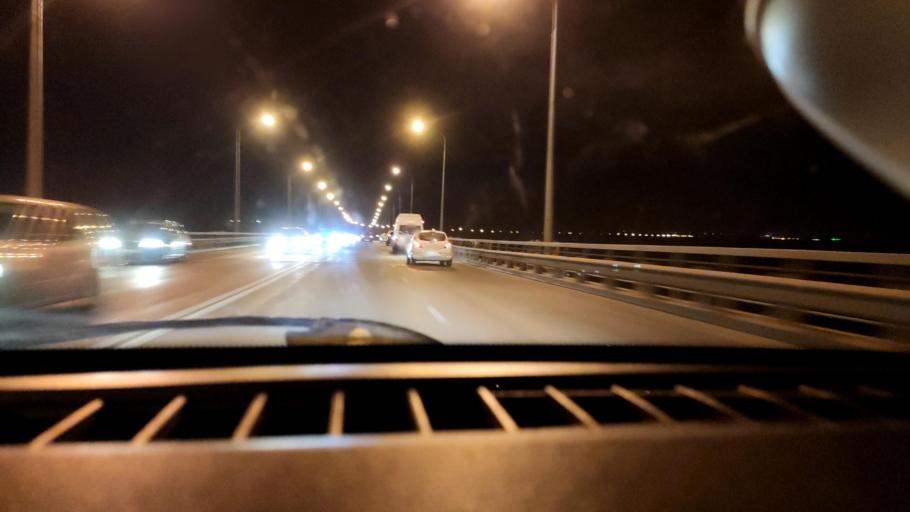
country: RU
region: Samara
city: Samara
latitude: 53.1701
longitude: 50.1953
